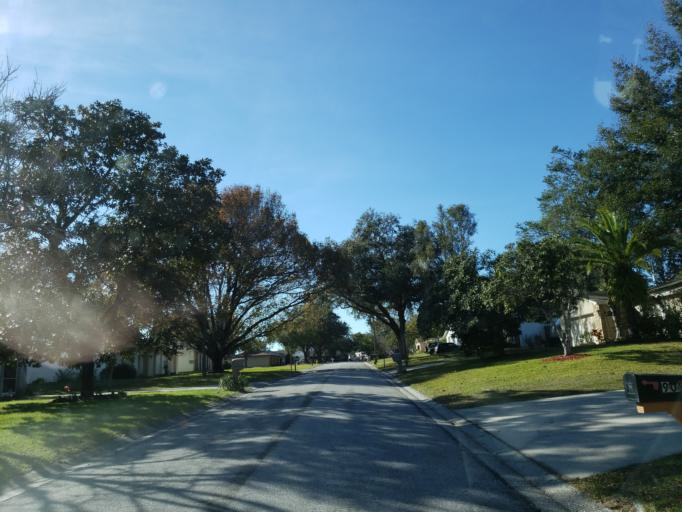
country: US
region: Florida
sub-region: Hillsborough County
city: Bloomingdale
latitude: 27.9034
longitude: -82.2711
